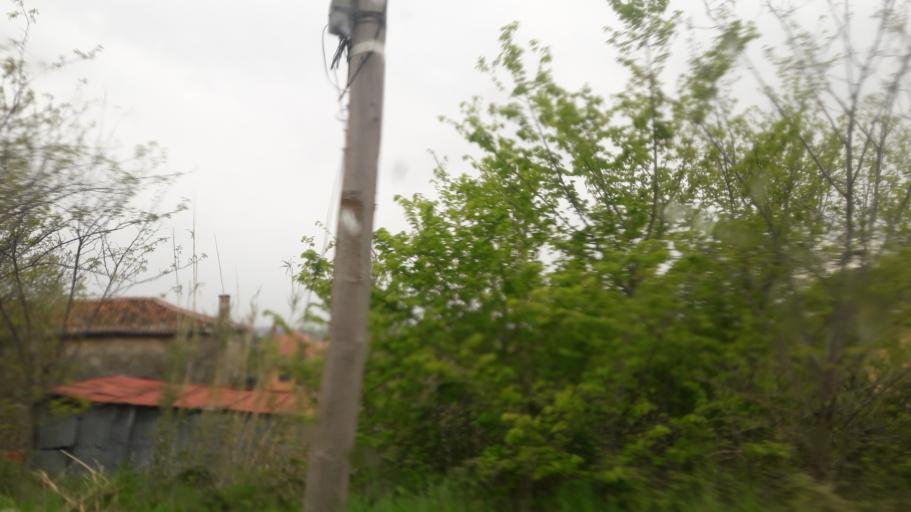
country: AL
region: Shkoder
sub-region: Rrethi i Shkodres
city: Berdica e Madhe
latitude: 41.9571
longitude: 19.5127
